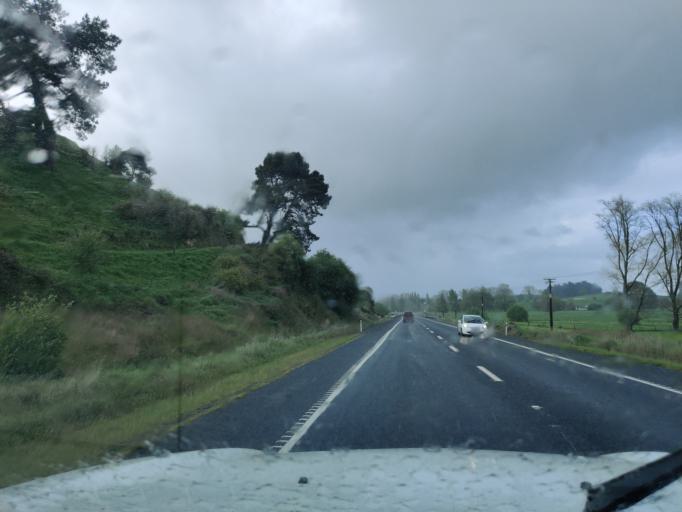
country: NZ
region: Waikato
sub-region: Matamata-Piako District
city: Matamata
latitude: -37.9707
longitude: 175.6918
